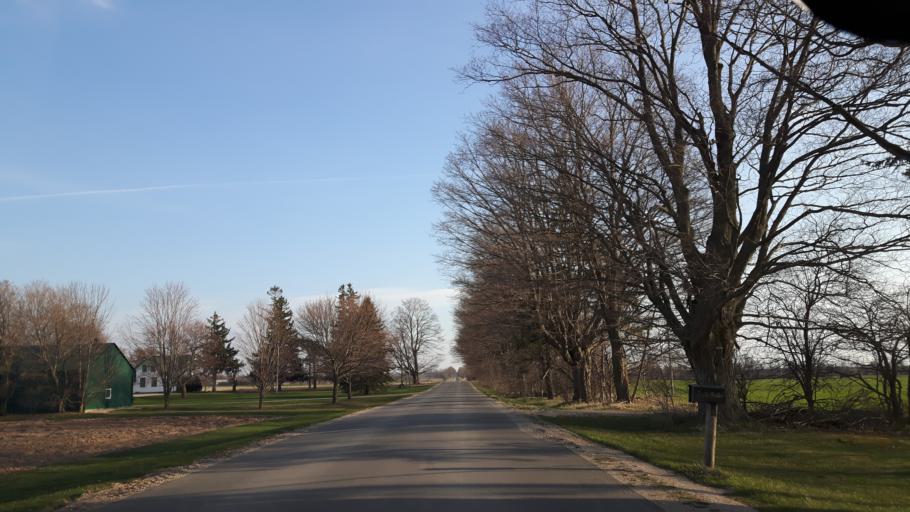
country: CA
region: Ontario
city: Goderich
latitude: 43.6397
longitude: -81.6643
